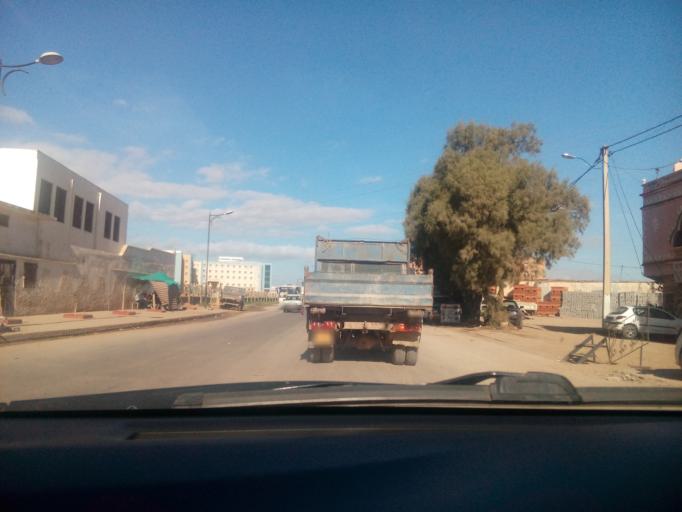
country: DZ
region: Oran
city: Sidi ech Chahmi
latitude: 35.6536
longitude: -0.5678
